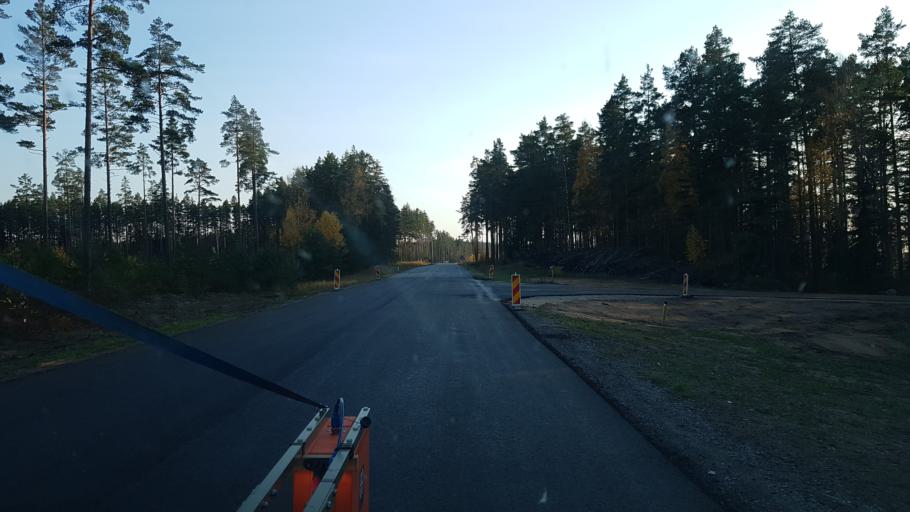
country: EE
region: Polvamaa
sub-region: Polva linn
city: Polva
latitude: 57.9259
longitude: 27.1825
